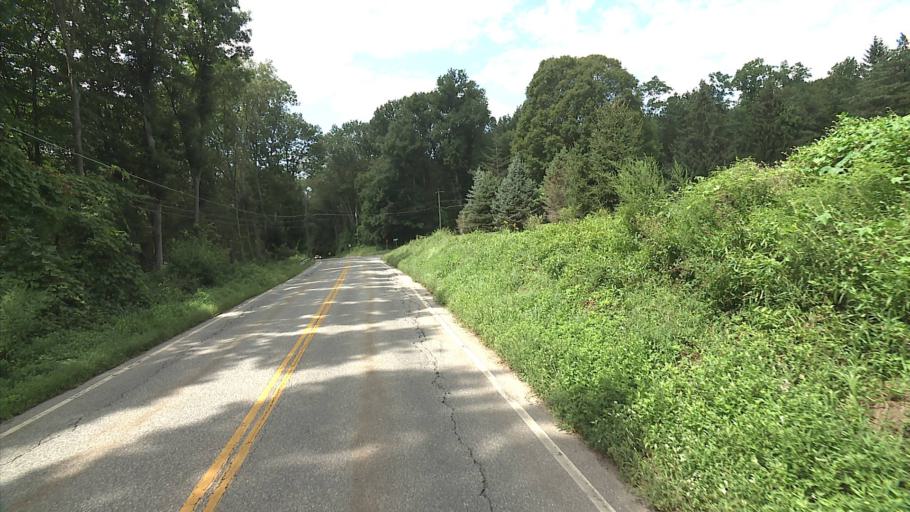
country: US
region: Connecticut
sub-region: Windham County
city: South Windham
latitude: 41.6429
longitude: -72.1872
